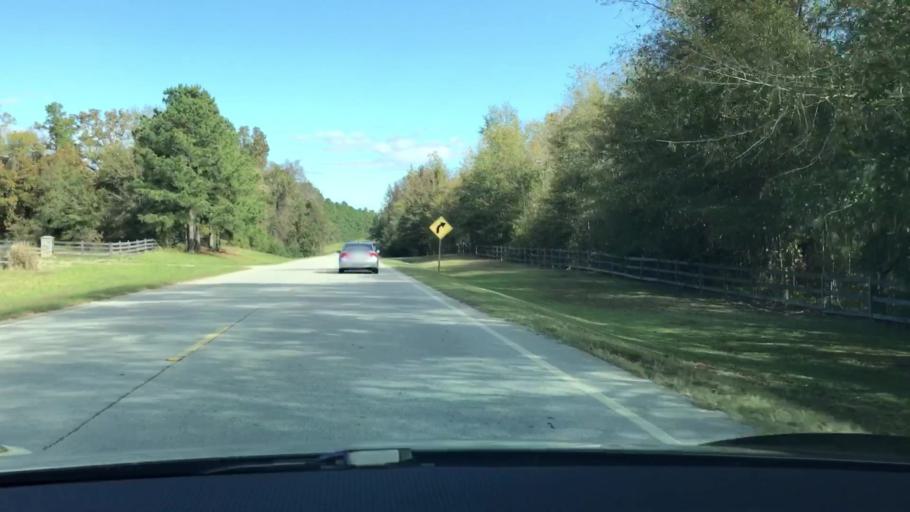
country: US
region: Georgia
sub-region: Jefferson County
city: Wrens
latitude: 33.2352
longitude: -82.4575
